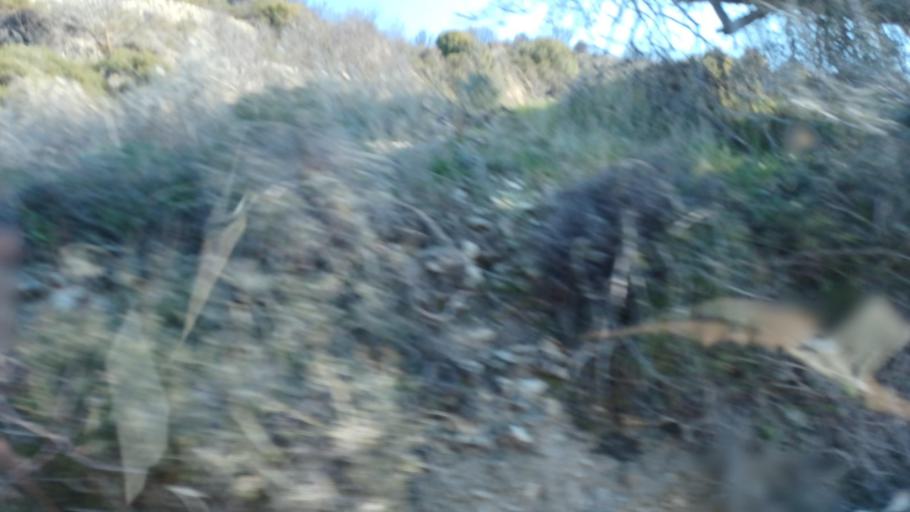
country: CY
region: Limassol
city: Pachna
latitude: 34.8246
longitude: 32.6866
